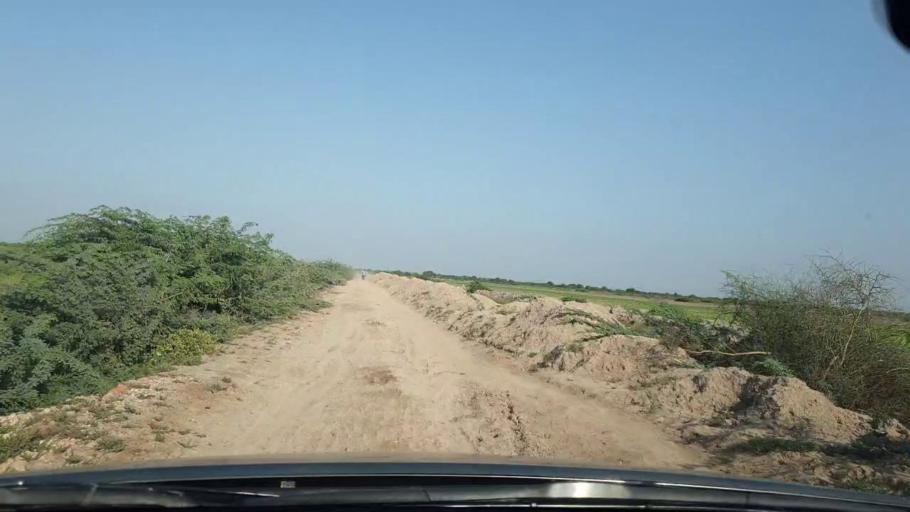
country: PK
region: Sindh
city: Naukot
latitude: 24.8336
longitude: 69.2497
